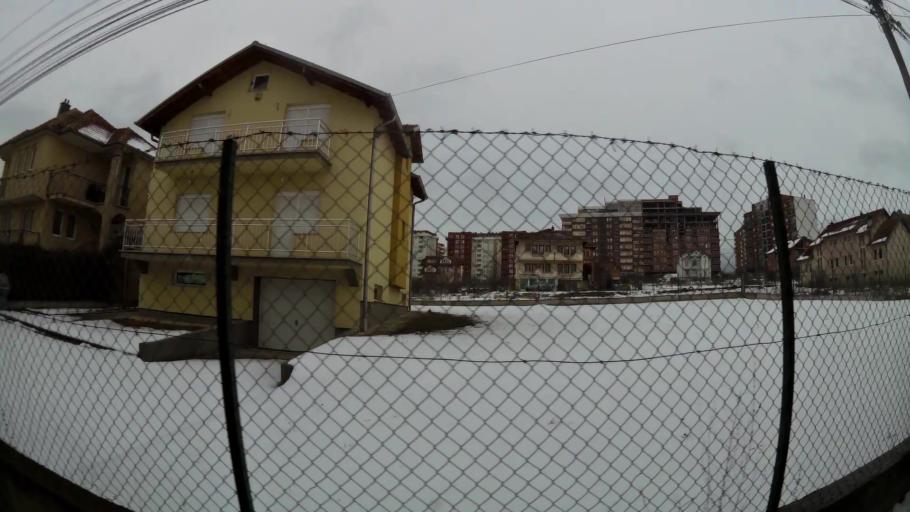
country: XK
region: Pristina
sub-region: Komuna e Prishtines
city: Pristina
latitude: 42.6473
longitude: 21.1794
